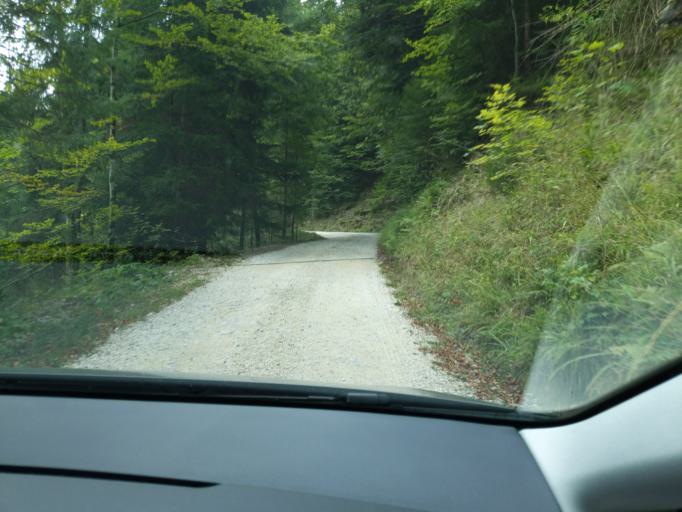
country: CH
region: Bern
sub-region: Oberaargau
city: Wyssachen
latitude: 47.0326
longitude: 7.8308
